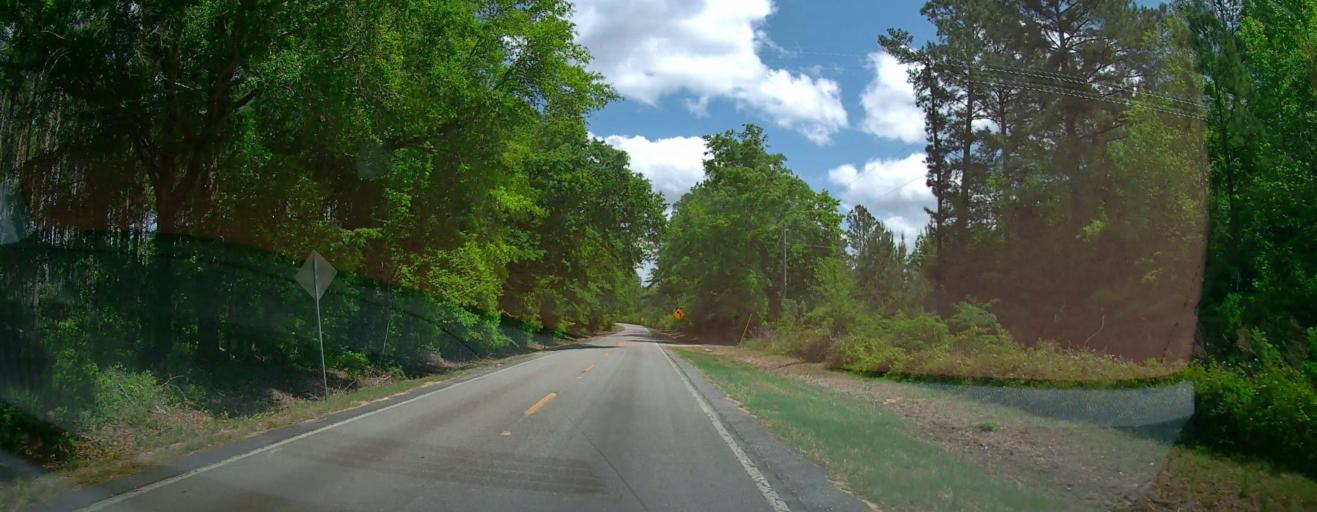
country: US
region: Georgia
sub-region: Bleckley County
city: Cochran
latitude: 32.4595
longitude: -83.2853
